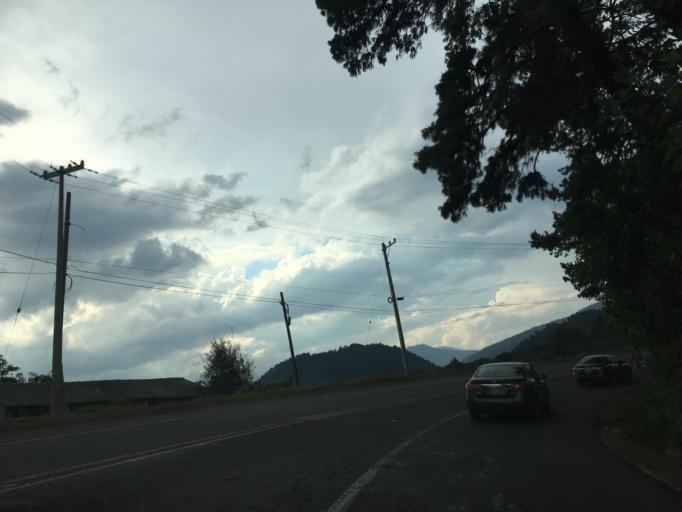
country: MX
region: Michoacan
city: Capacuaro
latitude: 19.5187
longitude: -102.0774
